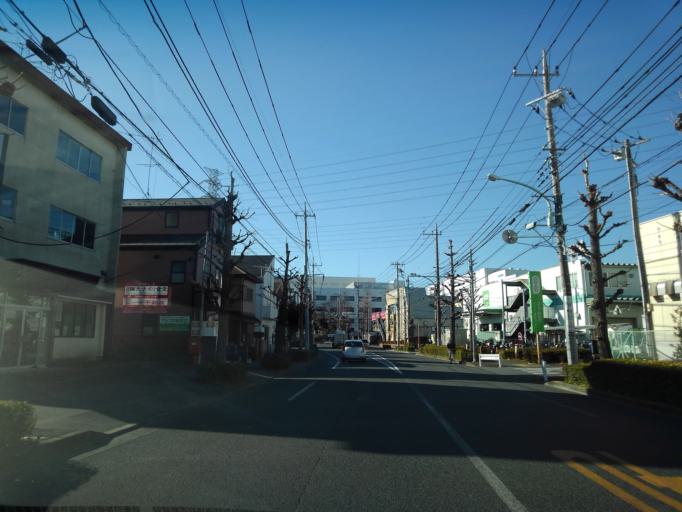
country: JP
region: Tokyo
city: Hino
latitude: 35.7190
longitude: 139.3824
